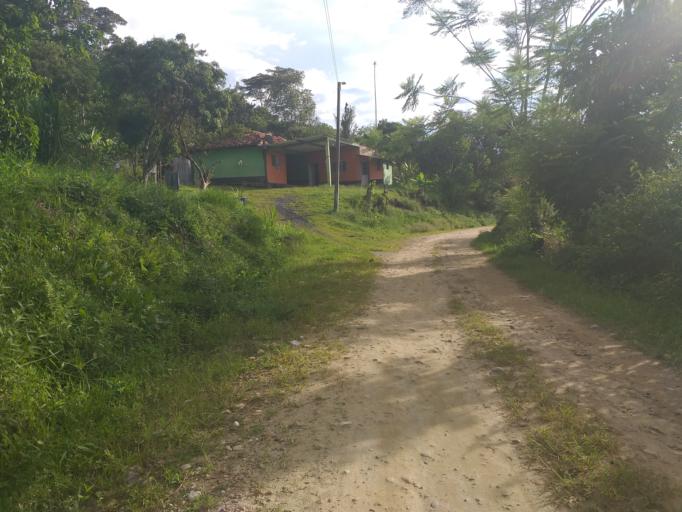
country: CO
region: Boyaca
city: Santana
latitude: 6.0533
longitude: -73.4883
